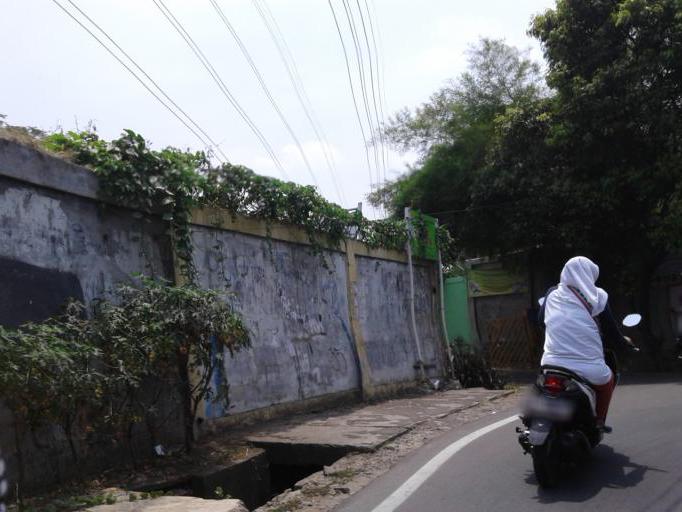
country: ID
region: West Java
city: Pamulang
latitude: -6.3160
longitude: 106.8165
